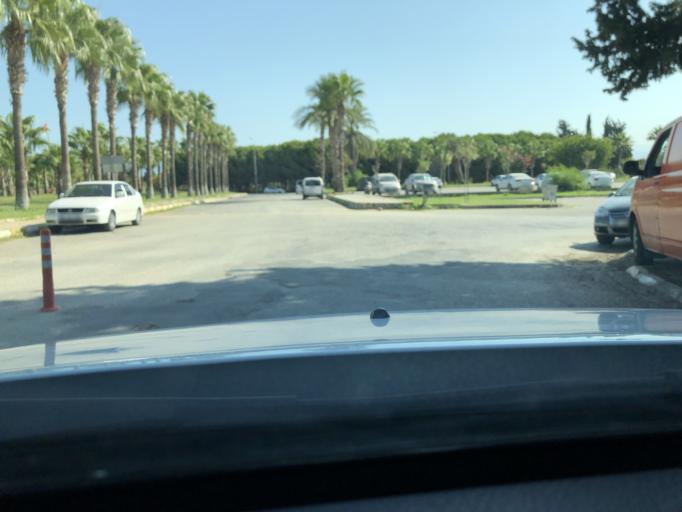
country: TR
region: Antalya
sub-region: Manavgat
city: Side
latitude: 36.7722
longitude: 31.3956
